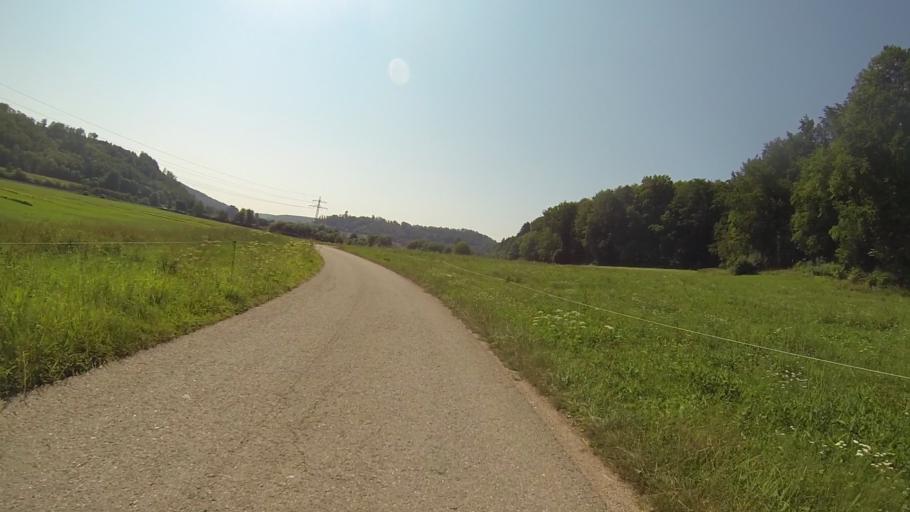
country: DE
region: Baden-Wuerttemberg
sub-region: Regierungsbezirk Stuttgart
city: Konigsbronn
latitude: 48.7514
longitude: 10.0966
